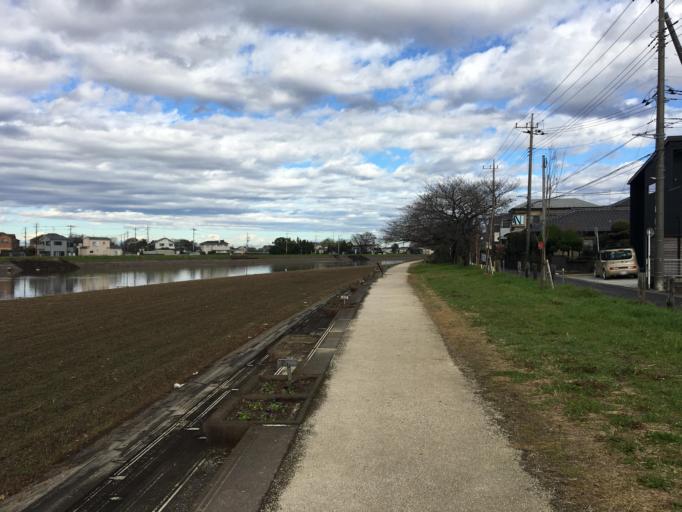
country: JP
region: Saitama
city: Koshigaya
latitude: 35.9217
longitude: 139.8052
